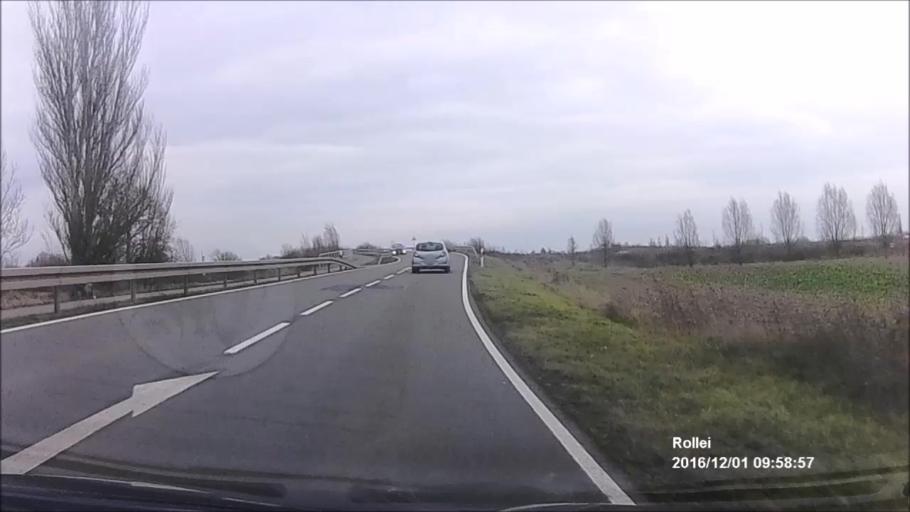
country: DE
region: Thuringia
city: Elxleben
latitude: 51.0285
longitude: 10.9751
